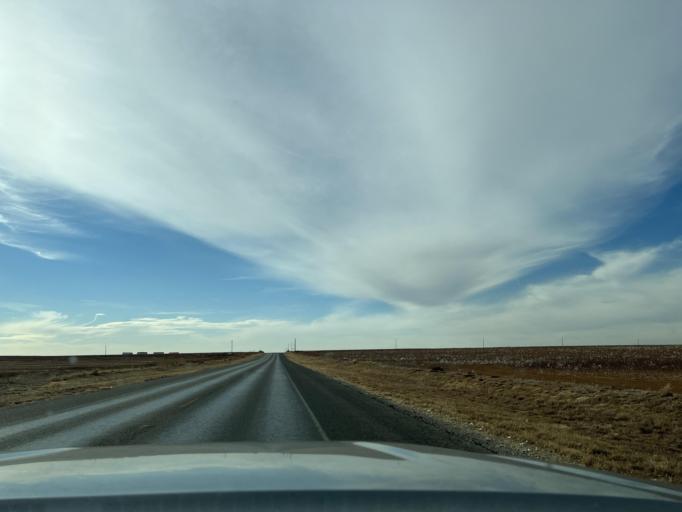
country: US
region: Texas
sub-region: Fisher County
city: Roby
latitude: 32.7416
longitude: -100.4520
